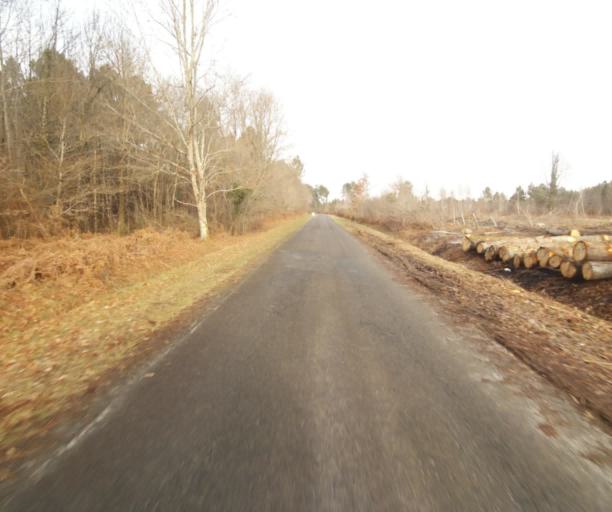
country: FR
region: Aquitaine
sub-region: Departement des Landes
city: Gabarret
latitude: 44.0872
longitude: 0.0704
